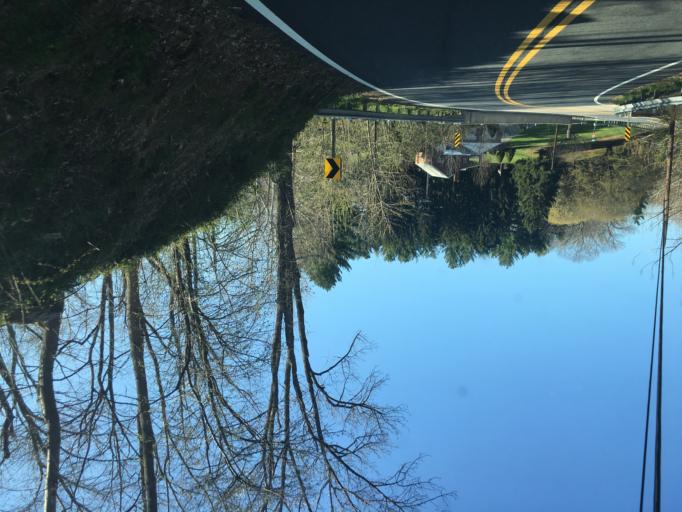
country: US
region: Maryland
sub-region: Frederick County
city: Myersville
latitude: 39.5168
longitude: -77.5477
